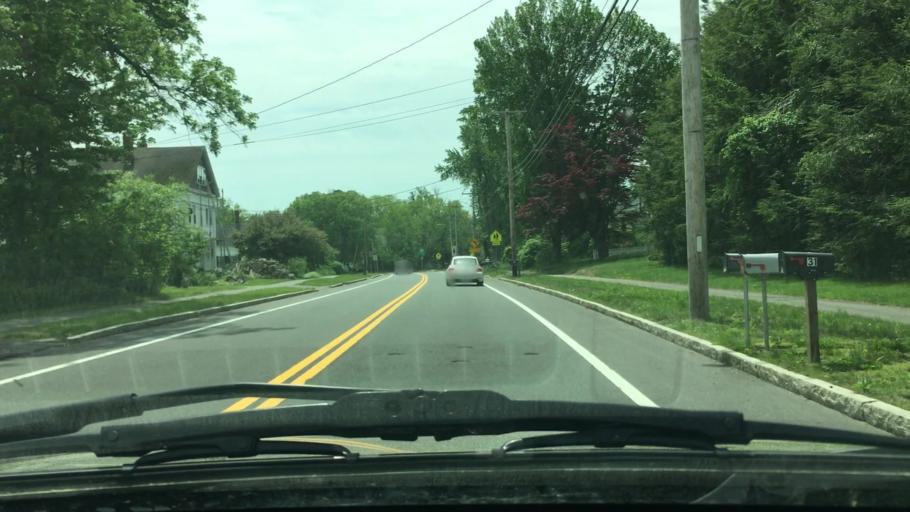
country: US
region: Massachusetts
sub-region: Hampshire County
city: Belchertown
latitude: 42.2749
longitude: -72.3995
